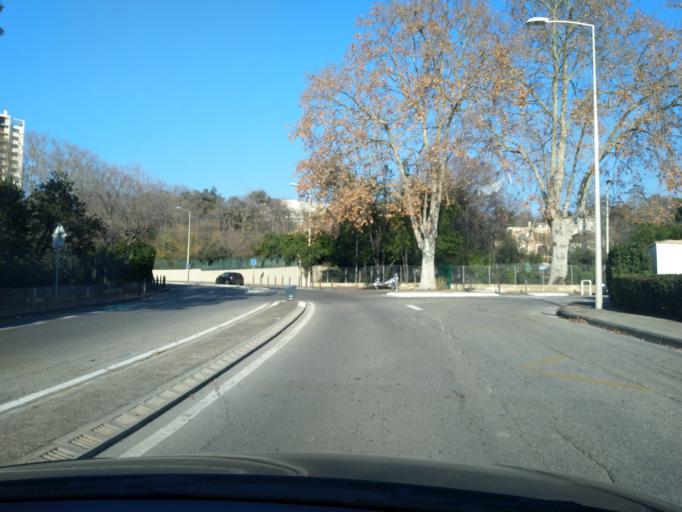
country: FR
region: Provence-Alpes-Cote d'Azur
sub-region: Departement des Bouches-du-Rhone
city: Marseille 12
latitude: 43.3012
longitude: 5.4312
